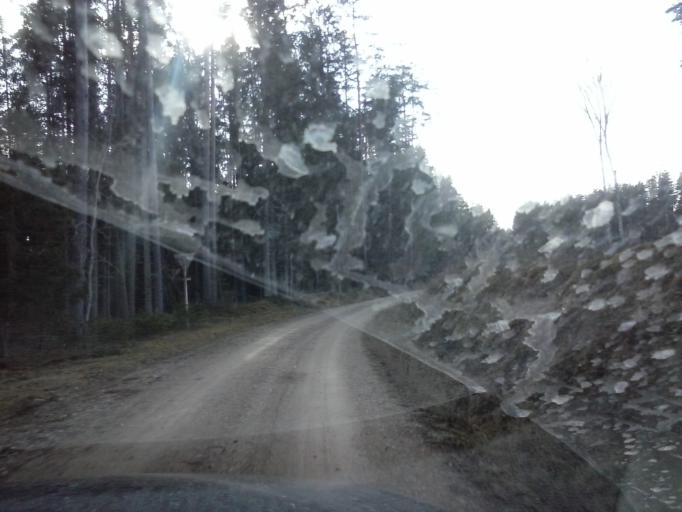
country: EE
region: Tartu
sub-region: Puhja vald
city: Puhja
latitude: 58.1596
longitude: 26.1481
